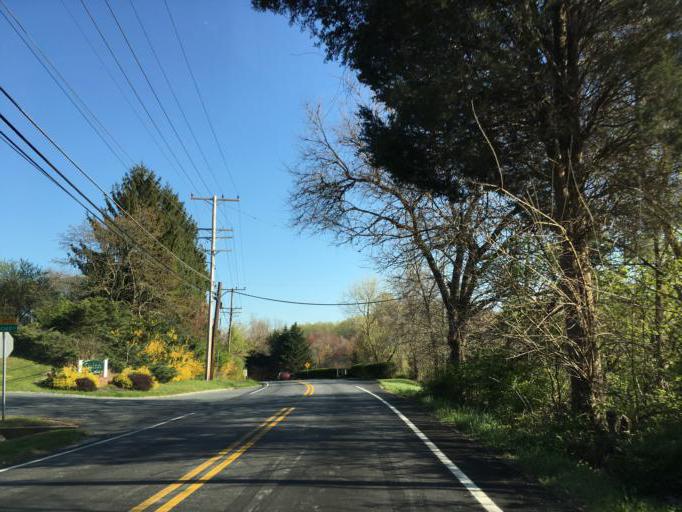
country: US
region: Maryland
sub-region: Baltimore County
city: Hampton
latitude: 39.5061
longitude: -76.5356
